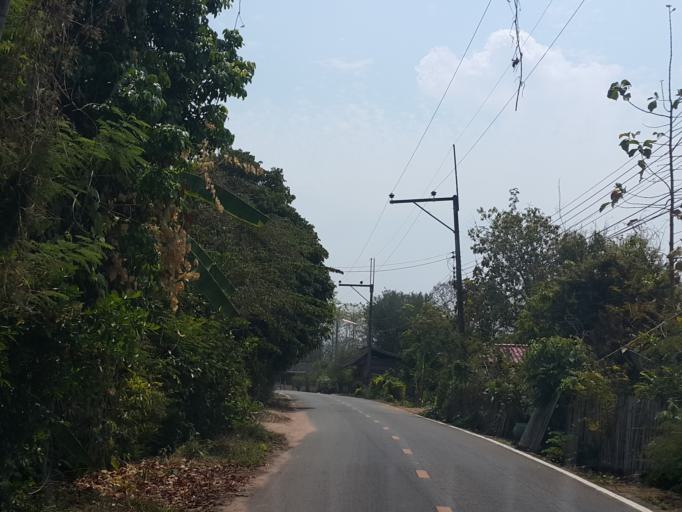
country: TH
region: Lampang
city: Mueang Pan
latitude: 18.7901
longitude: 99.4925
